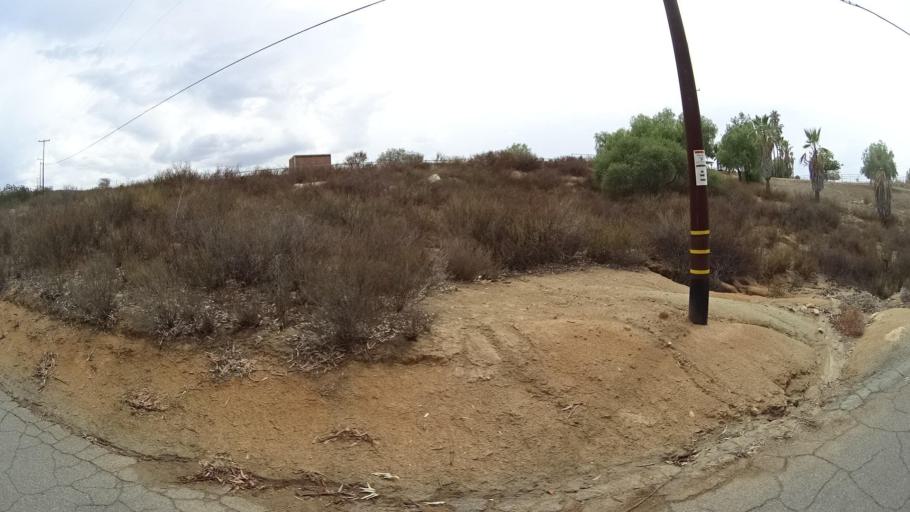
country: US
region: California
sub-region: San Diego County
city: Ramona
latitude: 33.0857
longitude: -116.8526
